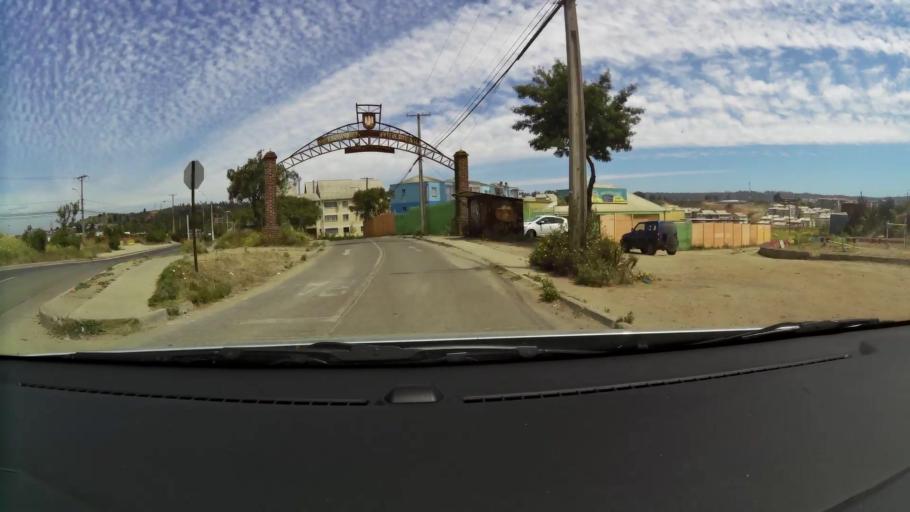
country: CL
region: Valparaiso
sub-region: Provincia de Valparaiso
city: Vina del Mar
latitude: -33.0585
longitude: -71.5594
